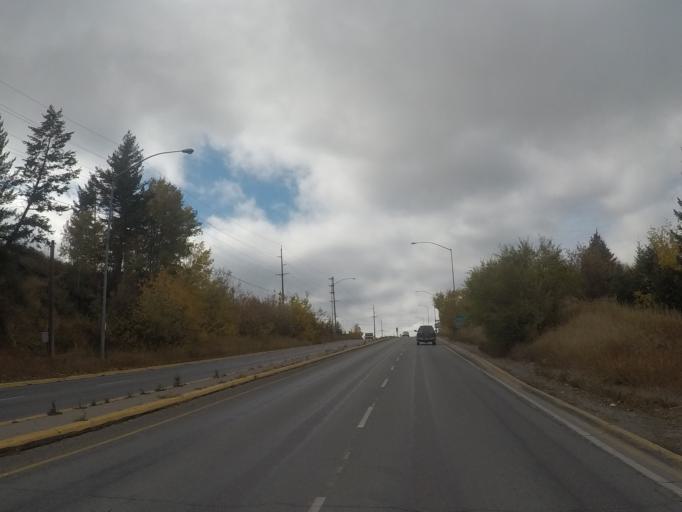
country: US
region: Montana
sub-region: Flathead County
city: Kalispell
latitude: 48.2049
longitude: -114.2982
